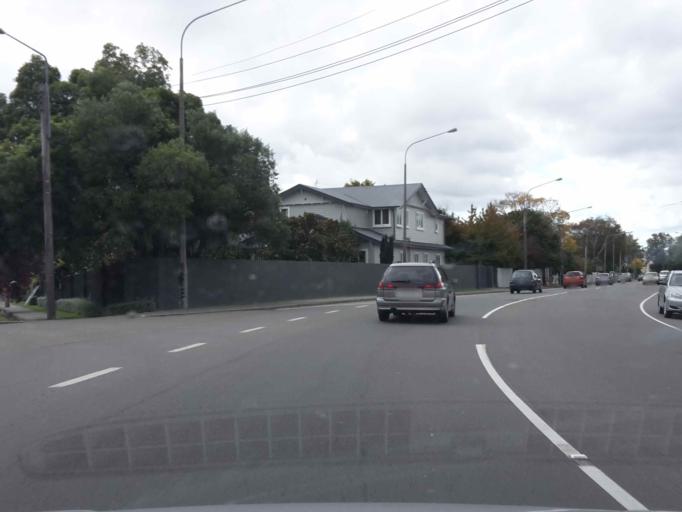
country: NZ
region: Canterbury
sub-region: Christchurch City
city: Christchurch
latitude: -43.5174
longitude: 172.6013
